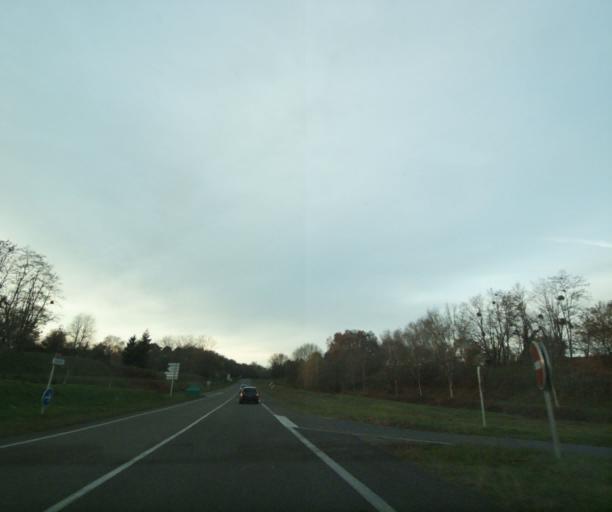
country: FR
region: Aquitaine
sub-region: Departement de la Gironde
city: Bazas
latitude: 44.4291
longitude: -0.2322
